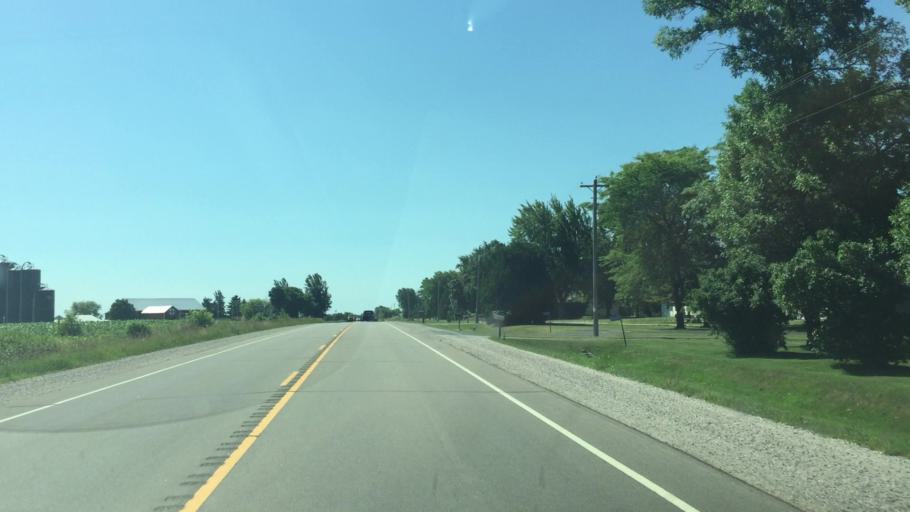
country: US
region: Wisconsin
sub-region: Calumet County
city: Chilton
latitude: 43.9924
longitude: -88.1253
